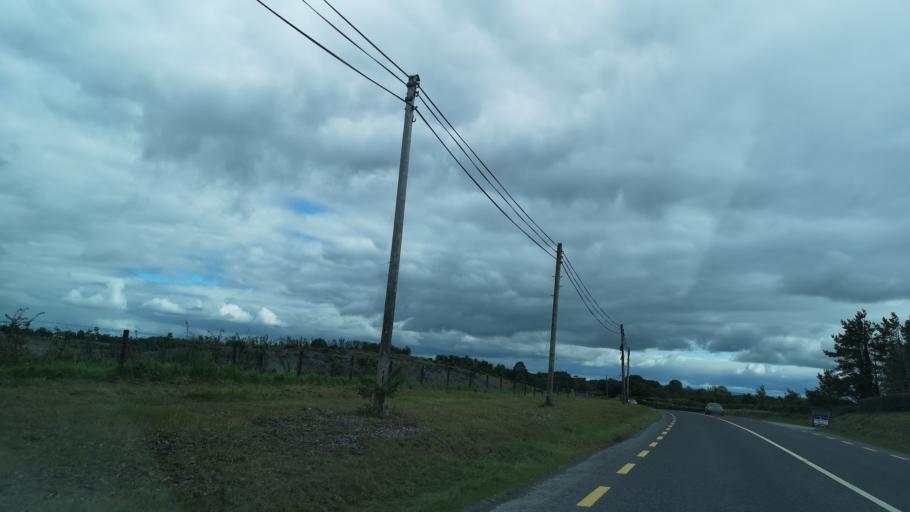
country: IE
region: Connaught
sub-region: County Galway
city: Ballinasloe
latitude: 53.3049
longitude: -8.1403
